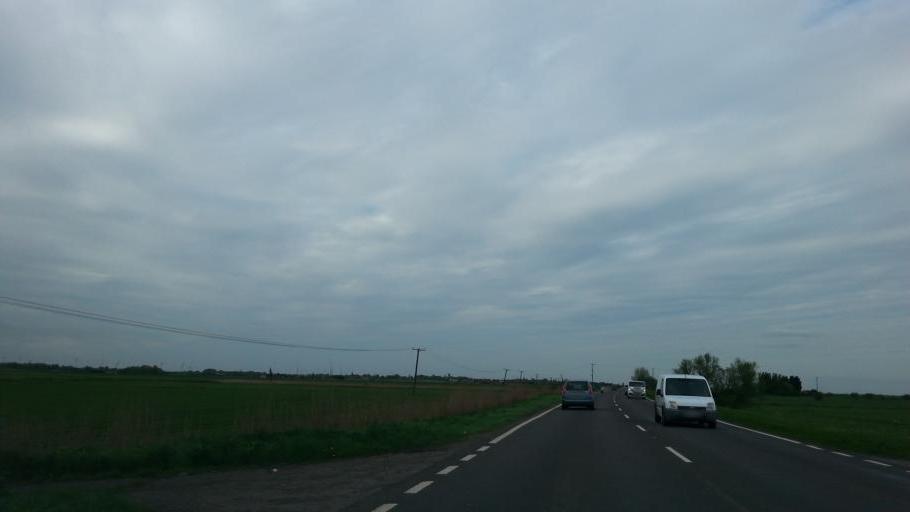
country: GB
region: England
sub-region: Cambridgeshire
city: Chatteris
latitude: 52.4680
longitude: 0.0456
